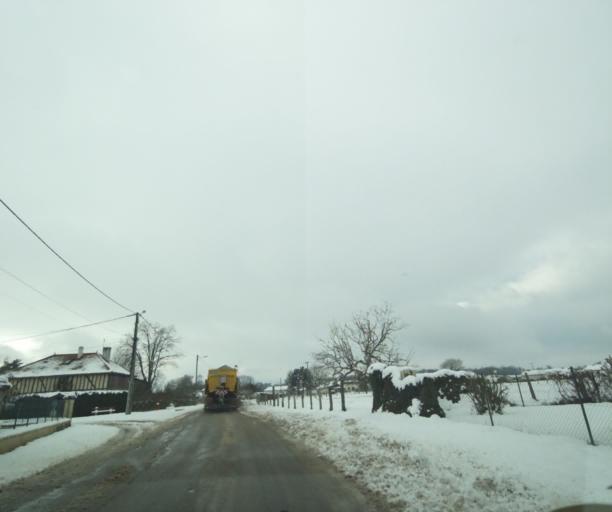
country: FR
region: Champagne-Ardenne
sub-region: Departement de la Haute-Marne
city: Montier-en-Der
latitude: 48.4925
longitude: 4.7000
